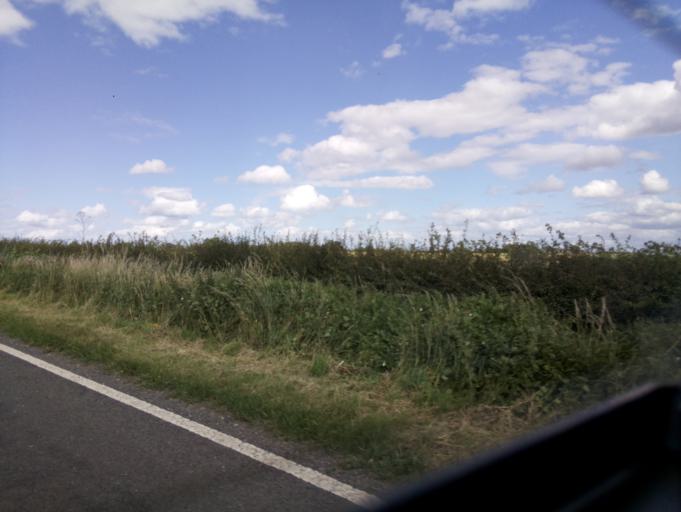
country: GB
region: England
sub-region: Nottinghamshire
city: Sutton Bonington
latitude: 52.8142
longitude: -1.2315
